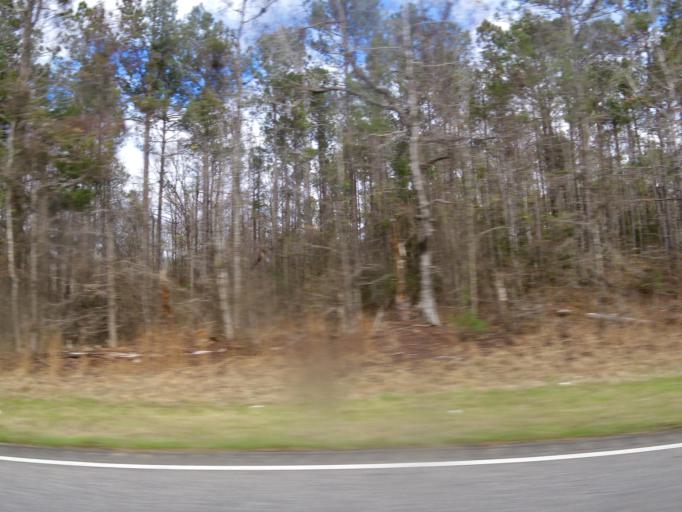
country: US
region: Alabama
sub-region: Barbour County
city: Eufaula
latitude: 31.9947
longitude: -85.2750
